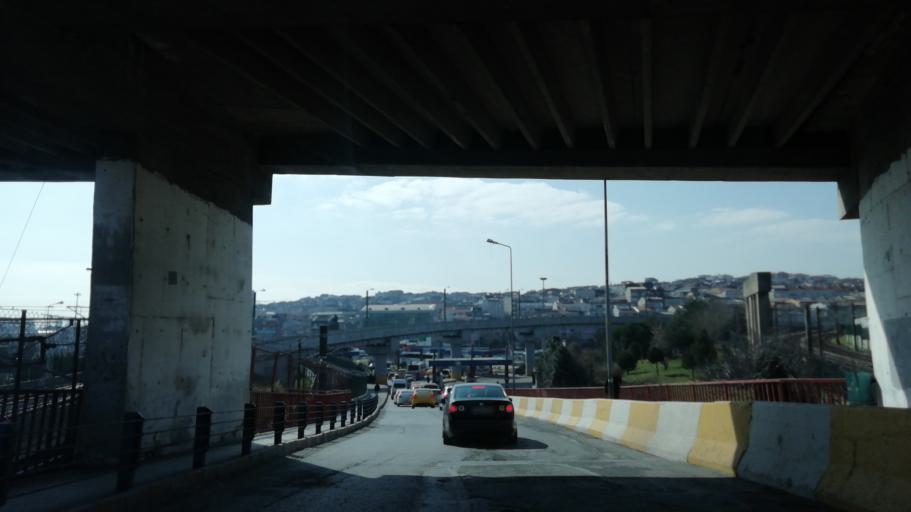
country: TR
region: Istanbul
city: Esenler
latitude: 41.0384
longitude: 28.8941
